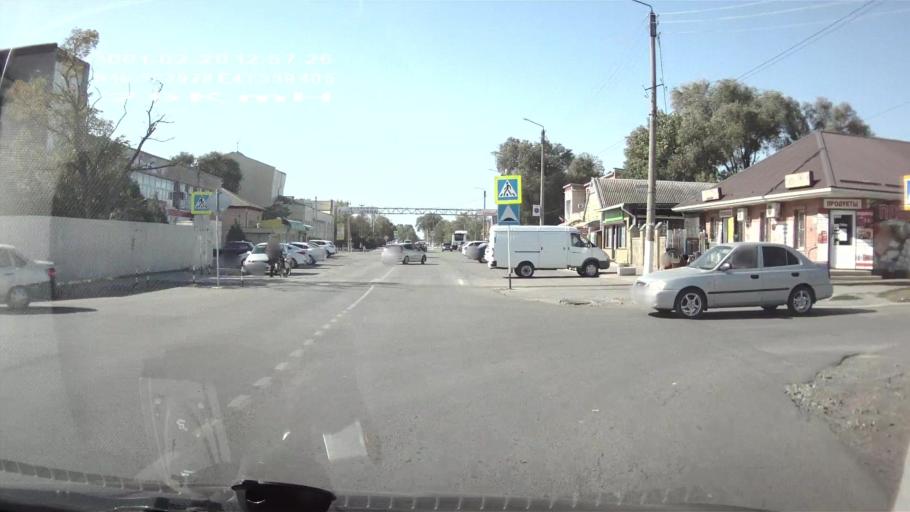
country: RU
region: Rostov
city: Gigant
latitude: 46.5081
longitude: 41.3394
